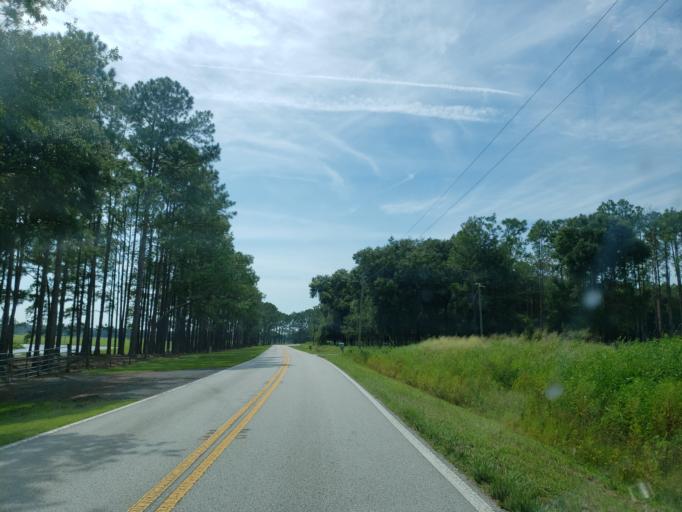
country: US
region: Florida
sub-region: Pasco County
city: San Antonio
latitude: 28.3910
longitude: -82.3071
